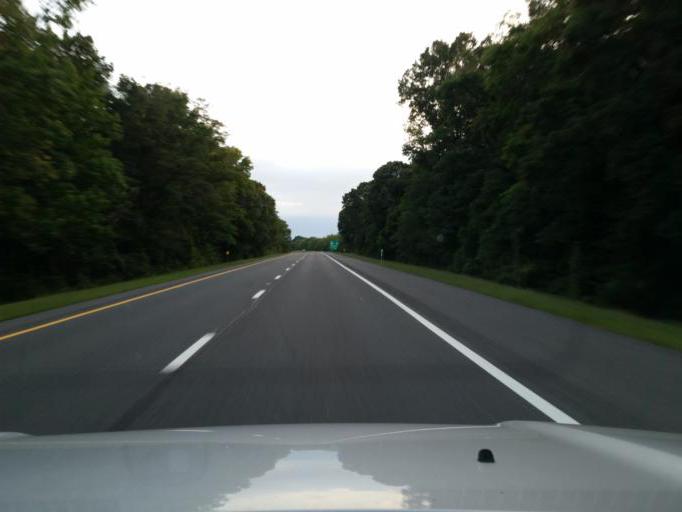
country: US
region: New Jersey
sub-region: Cape May County
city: Erma
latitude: 38.9763
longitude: -74.8924
